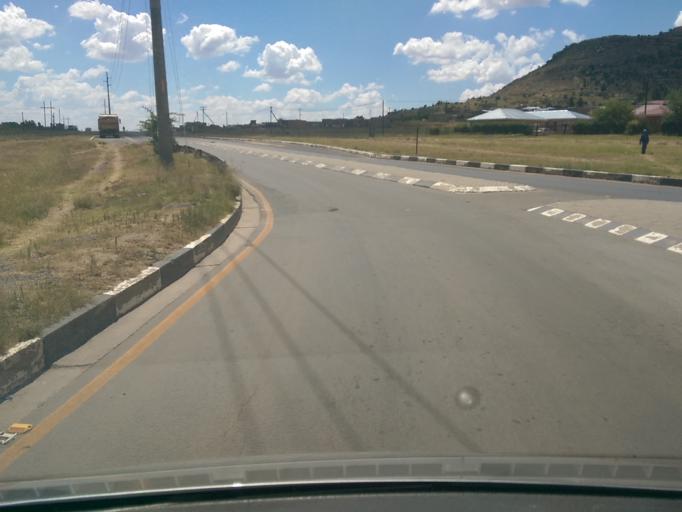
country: LS
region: Maseru
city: Maseru
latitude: -29.3647
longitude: 27.4692
